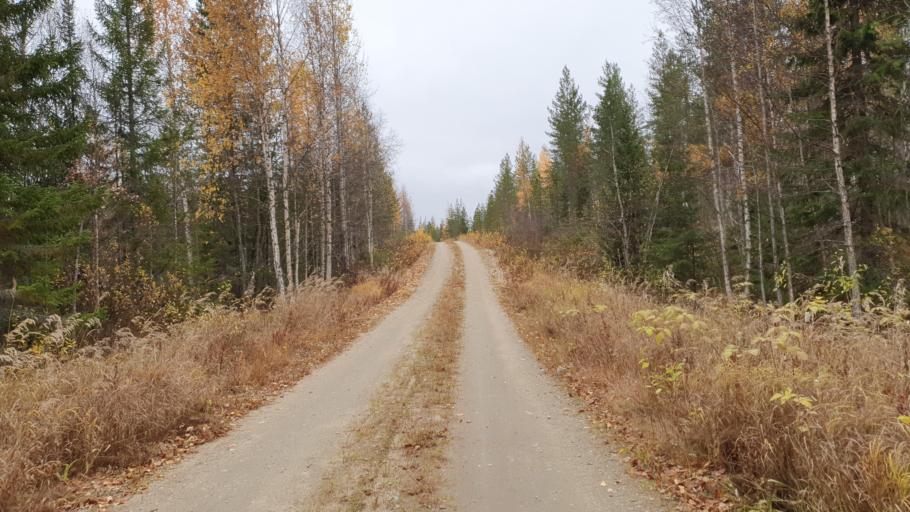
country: FI
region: Kainuu
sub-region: Kehys-Kainuu
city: Kuhmo
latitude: 64.4432
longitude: 29.6150
